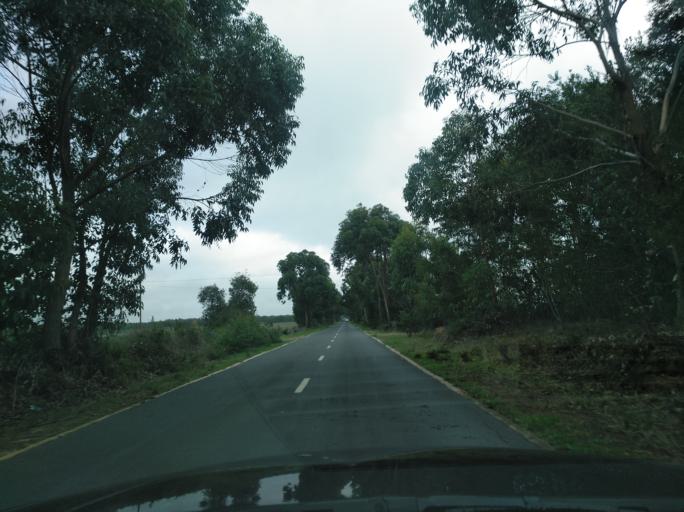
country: PT
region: Beja
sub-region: Odemira
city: Vila Nova de Milfontes
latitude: 37.7116
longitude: -8.7774
